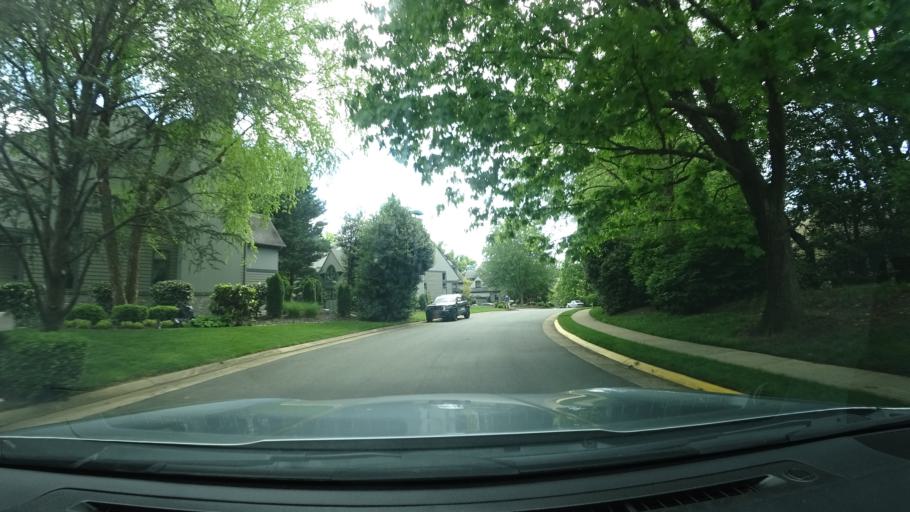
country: US
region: Virginia
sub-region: Fairfax County
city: Reston
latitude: 38.9762
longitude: -77.3405
